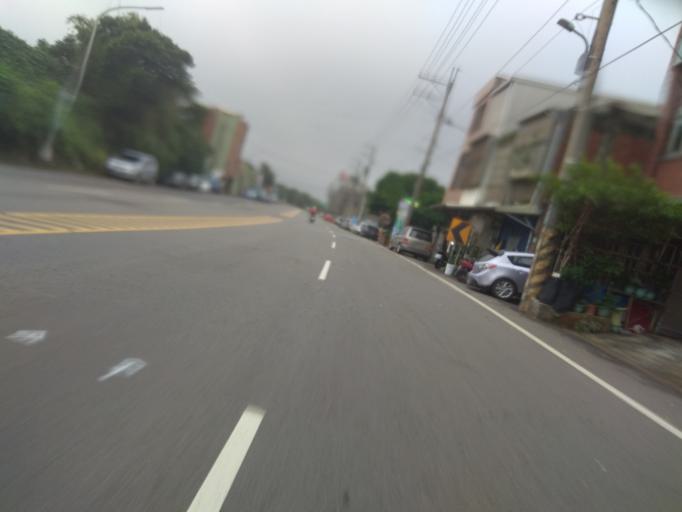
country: TW
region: Taiwan
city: Taoyuan City
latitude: 25.0318
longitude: 121.1014
